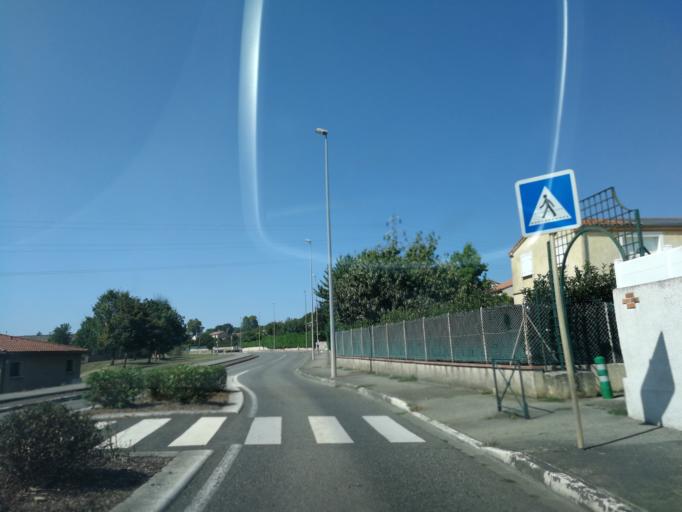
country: FR
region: Midi-Pyrenees
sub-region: Departement de la Haute-Garonne
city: Saint-Orens-de-Gameville
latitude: 43.5819
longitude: 1.5349
